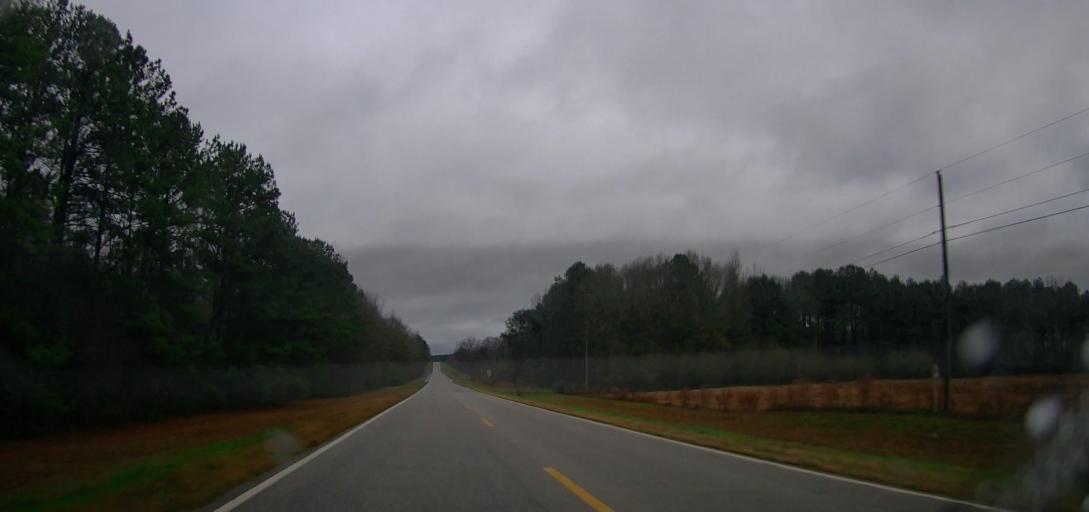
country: US
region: Alabama
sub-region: Bibb County
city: Centreville
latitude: 32.8465
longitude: -86.9602
